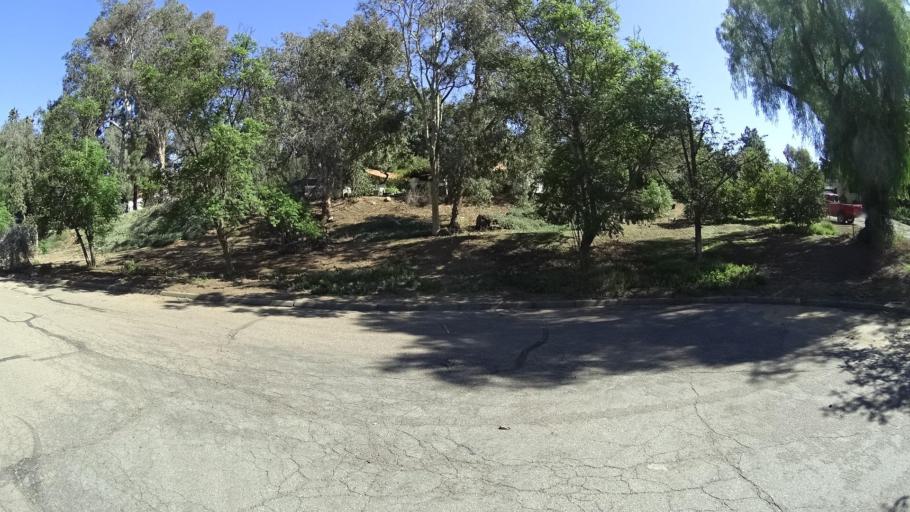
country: US
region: California
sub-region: San Diego County
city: Rancho San Diego
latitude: 32.7294
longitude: -116.9138
